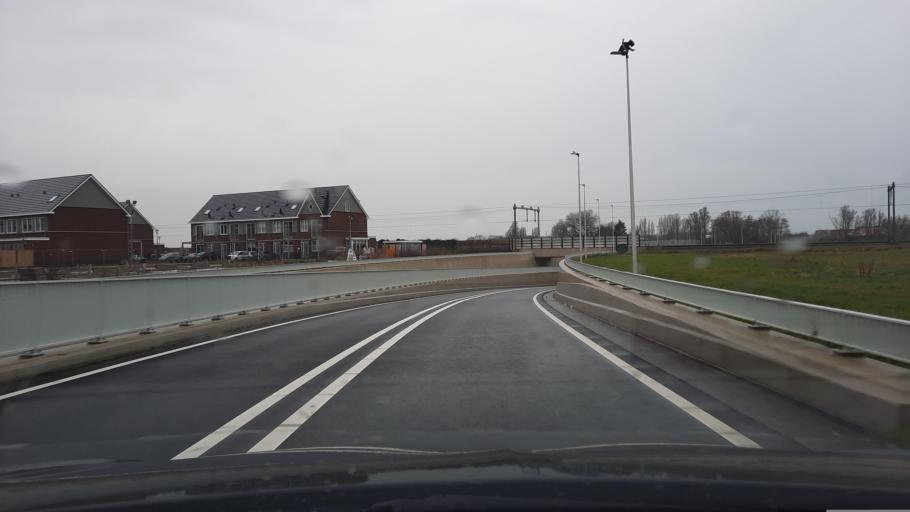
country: NL
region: South Holland
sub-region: Gemeente Teylingen
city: Voorhout
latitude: 52.2332
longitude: 4.4852
